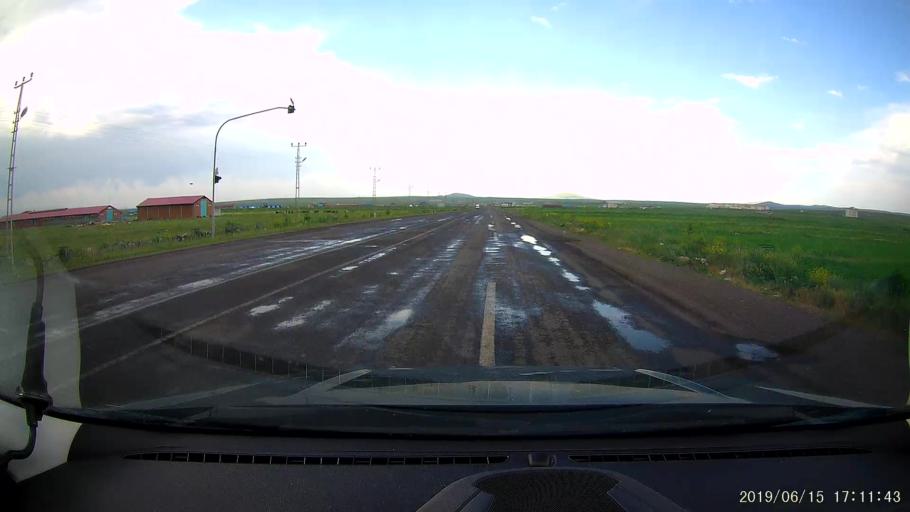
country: TR
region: Kars
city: Kars
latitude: 40.6140
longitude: 43.1371
